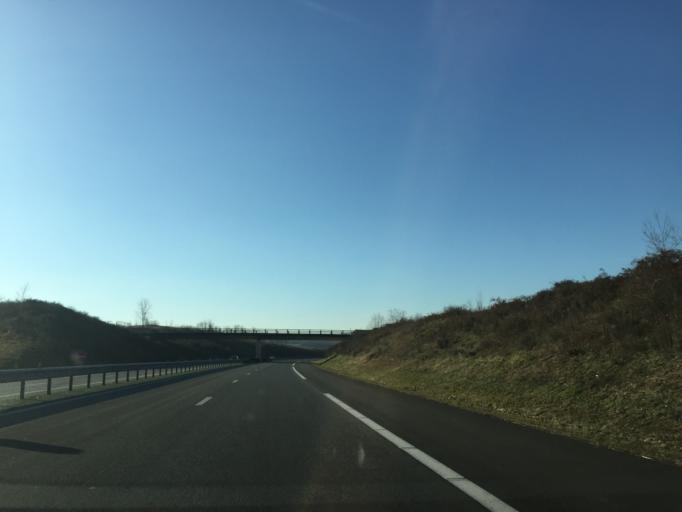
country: FR
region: Limousin
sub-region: Departement de la Correze
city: Mansac
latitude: 45.1546
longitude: 1.3846
